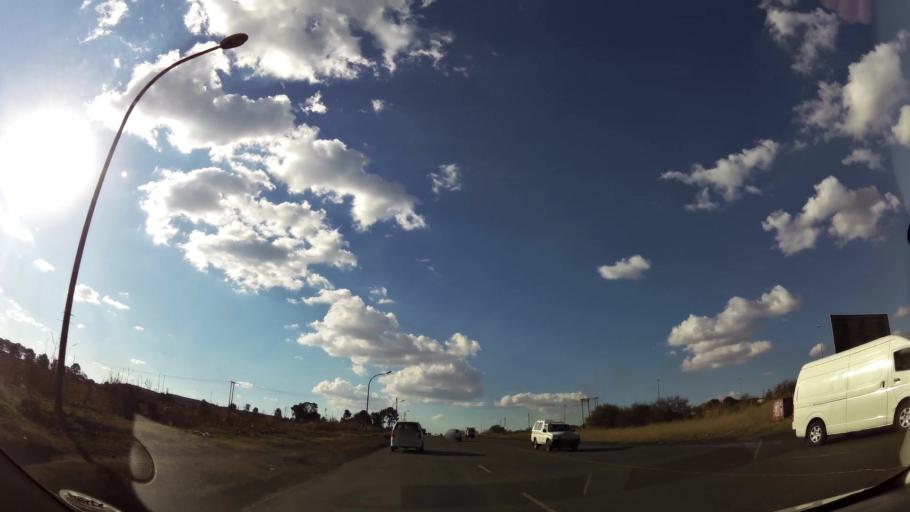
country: ZA
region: Mpumalanga
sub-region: Nkangala District Municipality
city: Witbank
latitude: -25.8763
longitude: 29.1651
